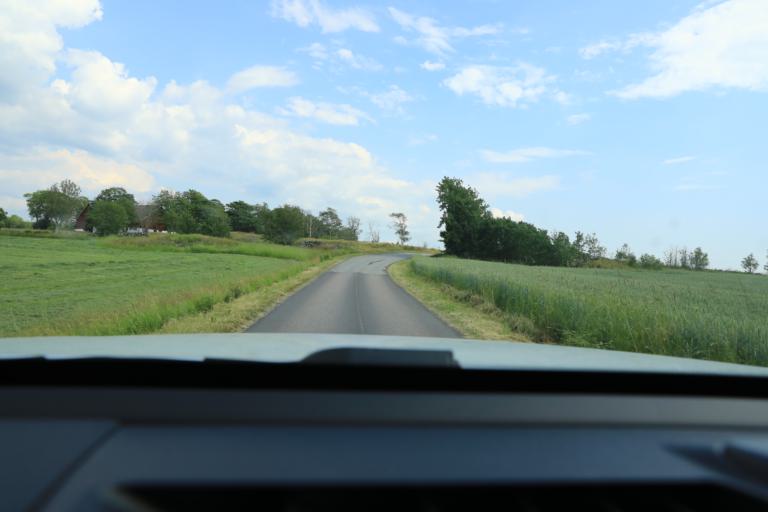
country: SE
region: Halland
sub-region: Varbergs Kommun
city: Varberg
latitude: 57.1381
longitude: 12.3266
